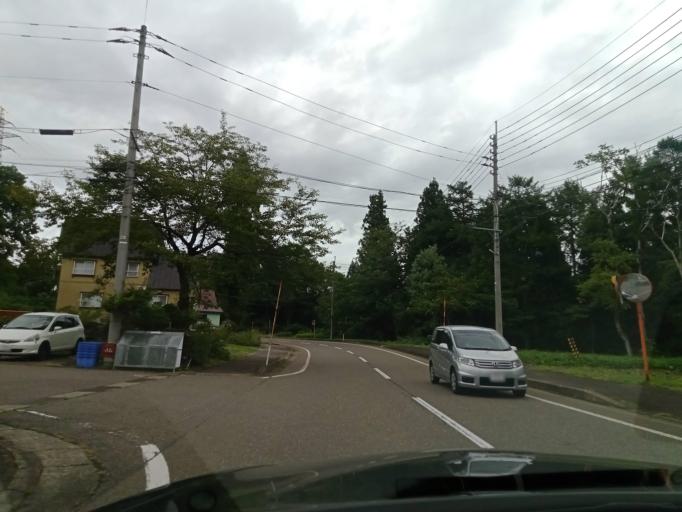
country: JP
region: Niigata
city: Arai
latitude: 36.8786
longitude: 138.1998
